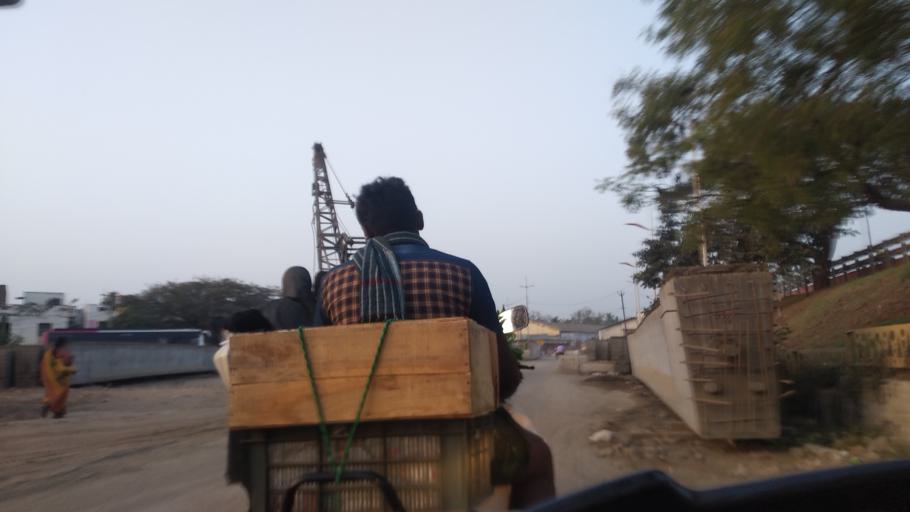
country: IN
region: Tamil Nadu
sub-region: Coimbatore
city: Coimbatore
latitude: 10.9795
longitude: 76.9608
